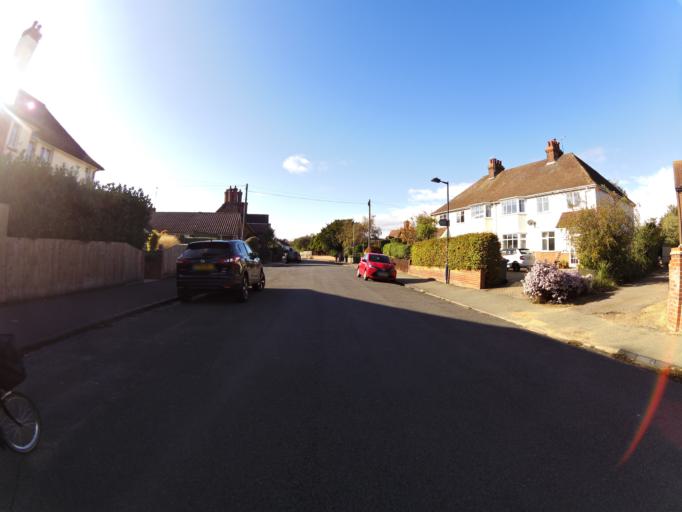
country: GB
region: England
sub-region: Suffolk
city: Felixstowe
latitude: 51.9660
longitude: 1.3607
